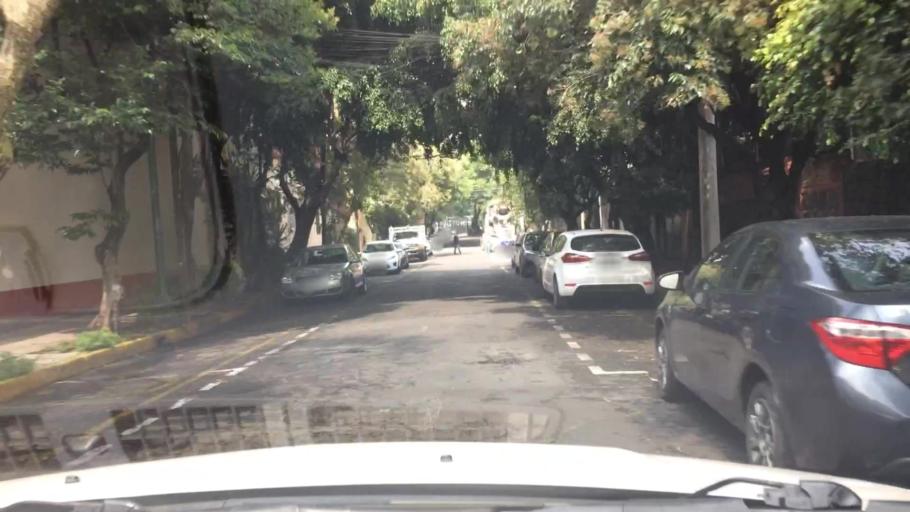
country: MX
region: Mexico City
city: Alvaro Obregon
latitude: 19.3685
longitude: -99.1865
